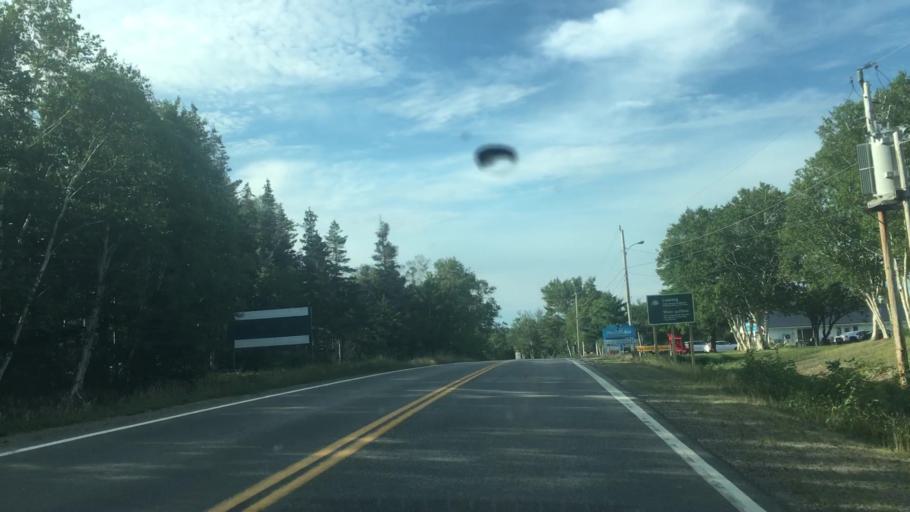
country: CA
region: Nova Scotia
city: Sydney Mines
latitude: 46.8191
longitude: -60.7957
